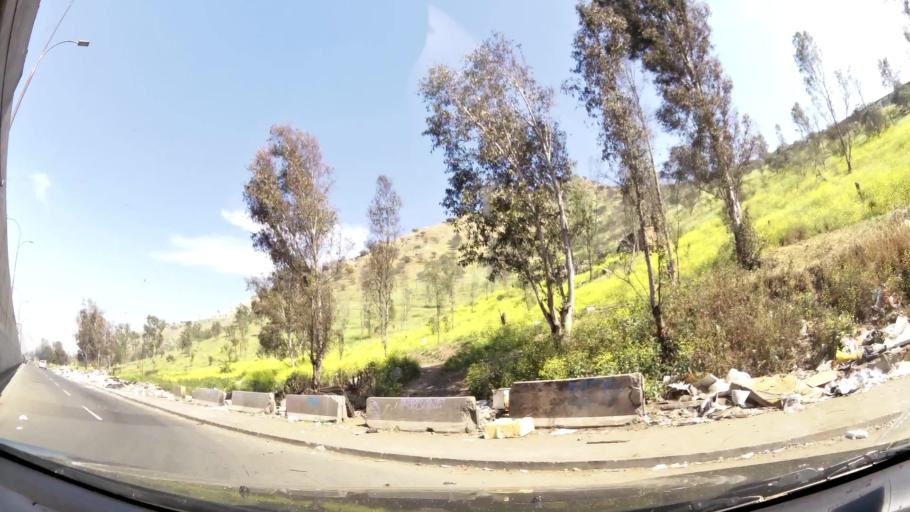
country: CL
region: Santiago Metropolitan
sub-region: Provincia de Santiago
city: Lo Prado
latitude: -33.3836
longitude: -70.6965
